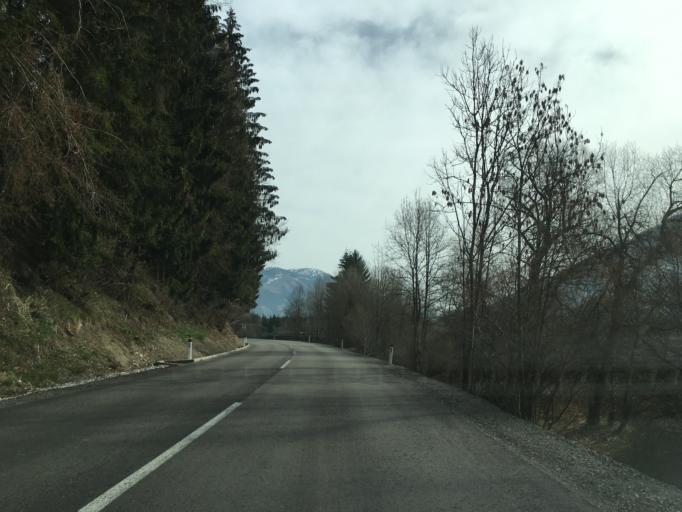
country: AT
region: Styria
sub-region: Politischer Bezirk Liezen
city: Selzthal
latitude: 47.5637
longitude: 14.3045
